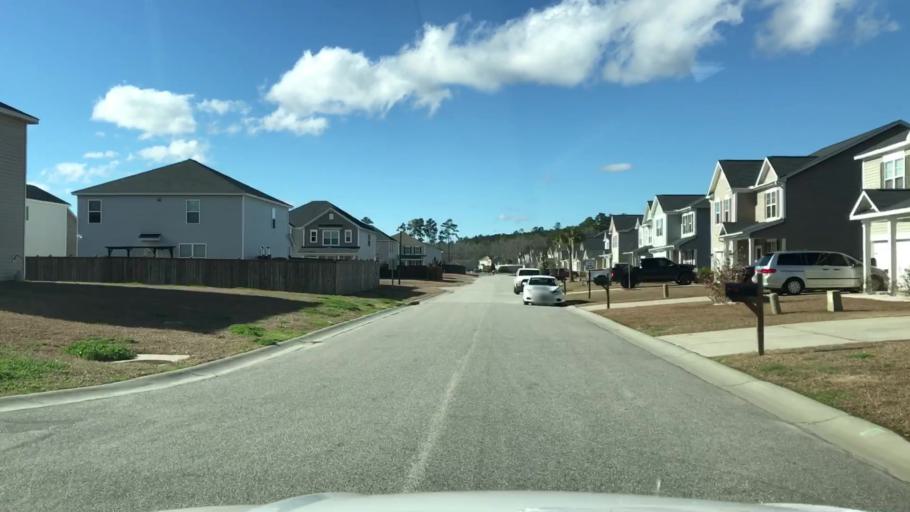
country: US
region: South Carolina
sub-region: Dorchester County
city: Summerville
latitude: 33.0898
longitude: -80.1928
